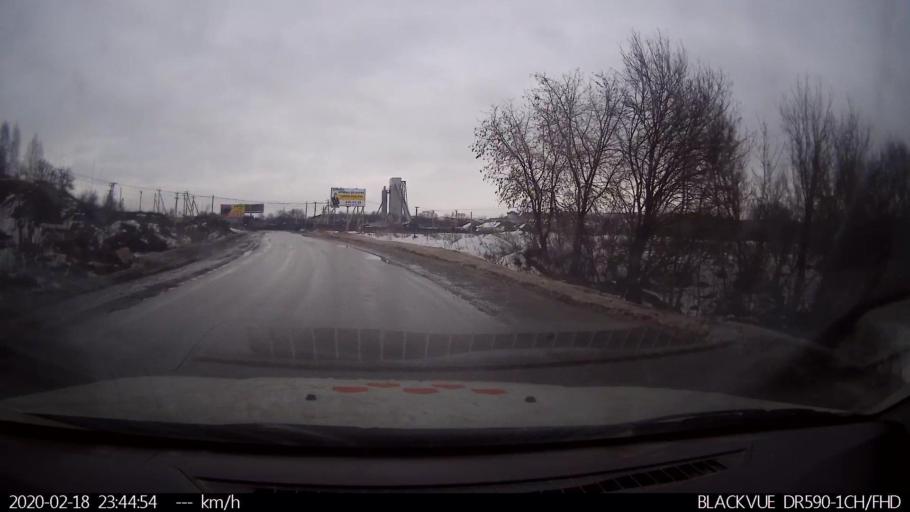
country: RU
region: Nizjnij Novgorod
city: Afonino
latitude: 56.2402
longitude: 44.0964
